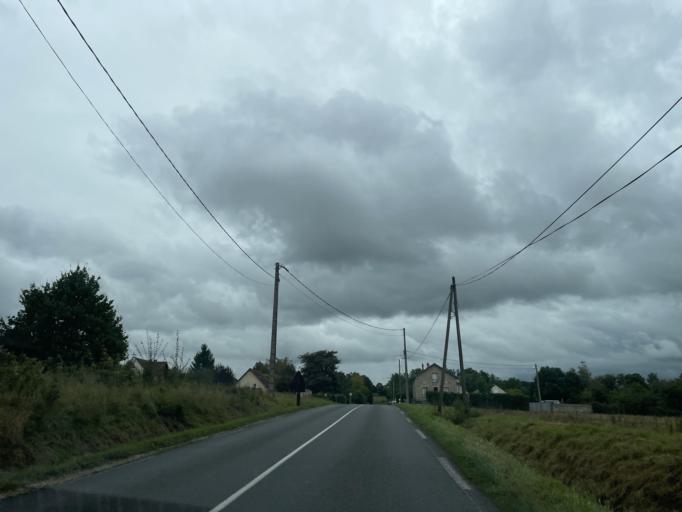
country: FR
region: Ile-de-France
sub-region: Departement de Seine-et-Marne
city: Boissy-le-Chatel
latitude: 48.8123
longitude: 3.1325
